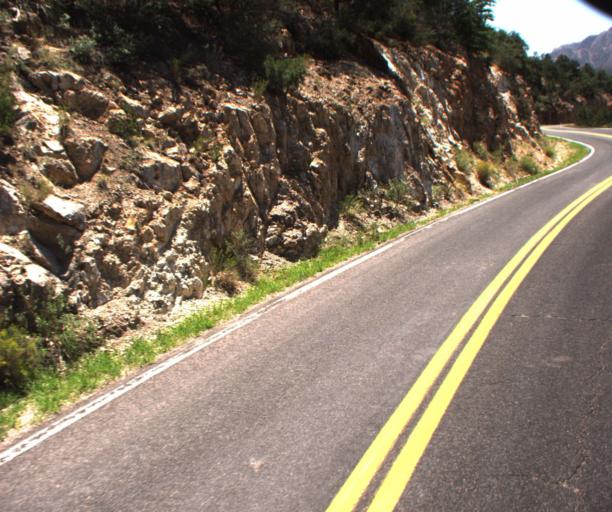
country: US
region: Arizona
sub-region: Greenlee County
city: Morenci
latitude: 33.1655
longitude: -109.3661
